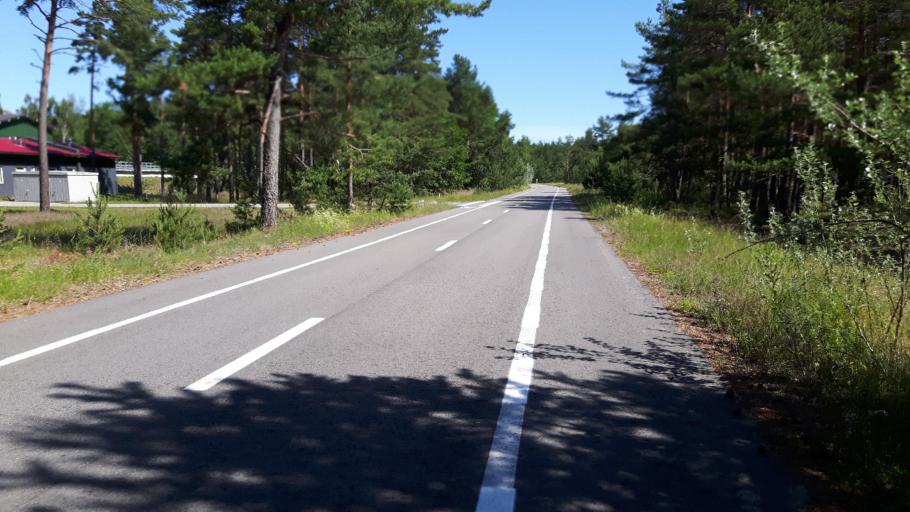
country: LT
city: Nida
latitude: 55.3236
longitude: 21.0255
